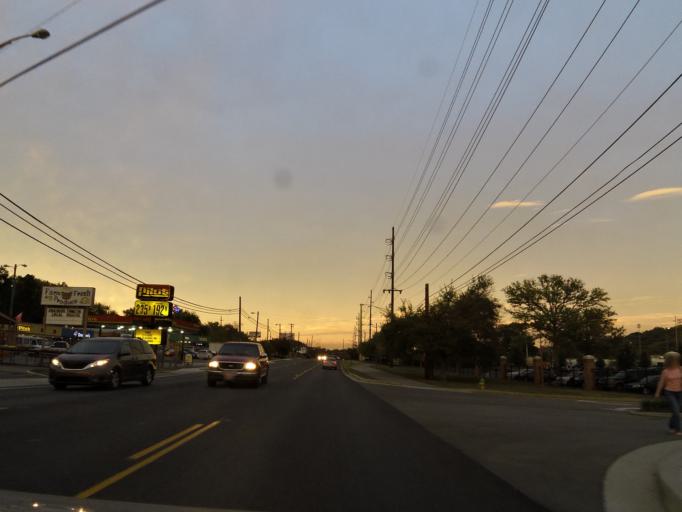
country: US
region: Tennessee
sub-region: Knox County
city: Knoxville
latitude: 35.9465
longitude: -83.9799
